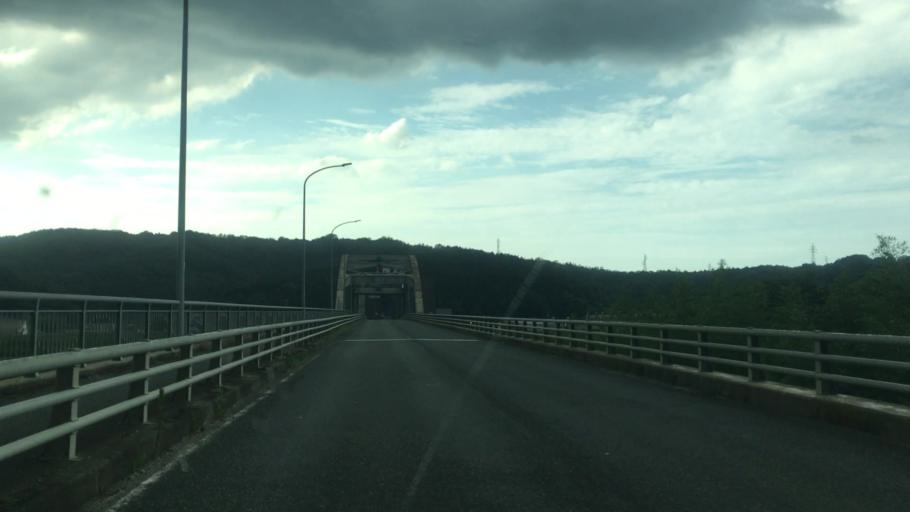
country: JP
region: Hyogo
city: Toyooka
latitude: 35.5047
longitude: 134.8171
